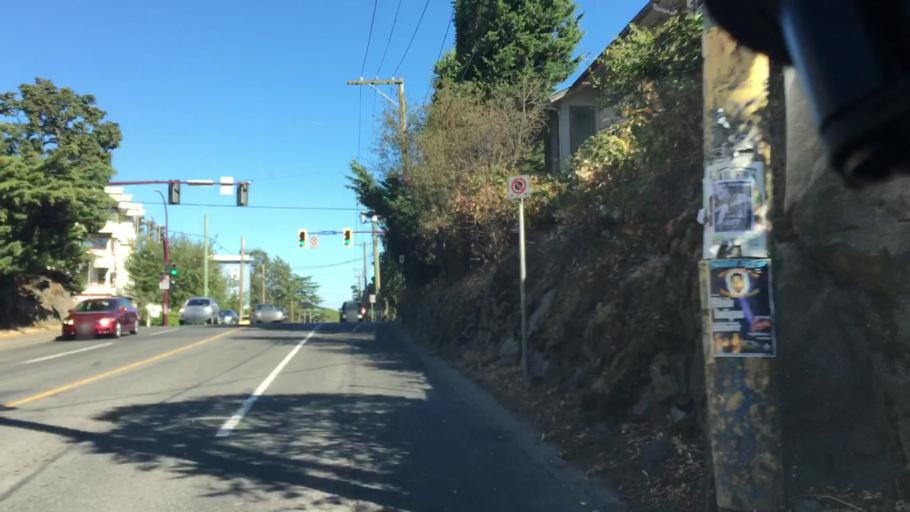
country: CA
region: British Columbia
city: Victoria
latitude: 48.4353
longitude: -123.3588
